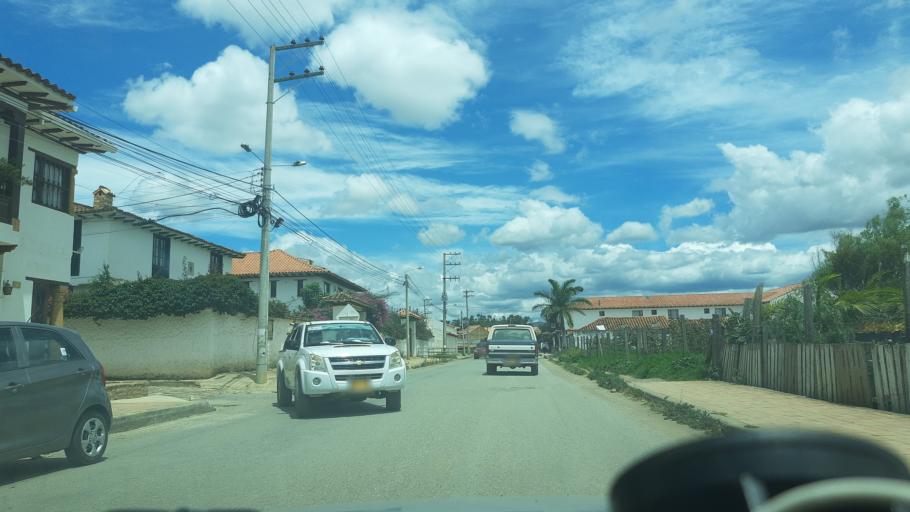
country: CO
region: Boyaca
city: Villa de Leiva
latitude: 5.6358
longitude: -73.5277
